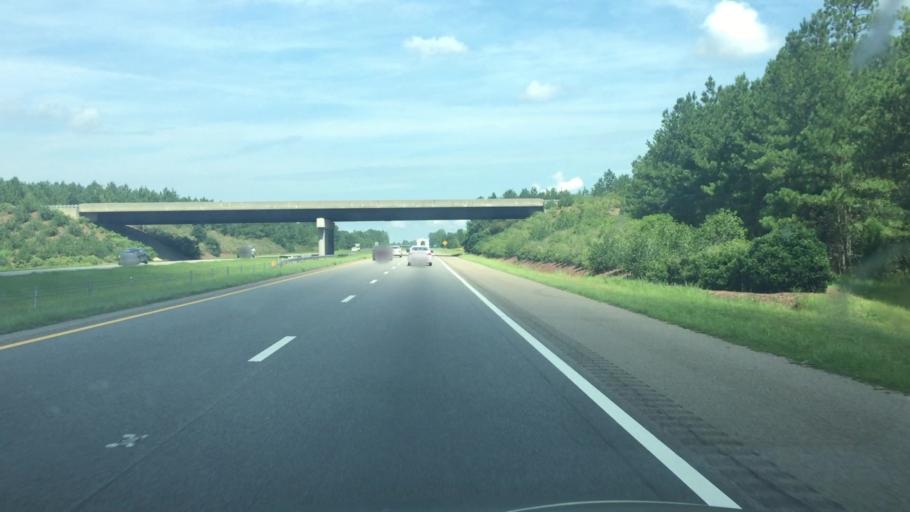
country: US
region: North Carolina
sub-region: Richmond County
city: Hamlet
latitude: 34.8577
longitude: -79.7418
